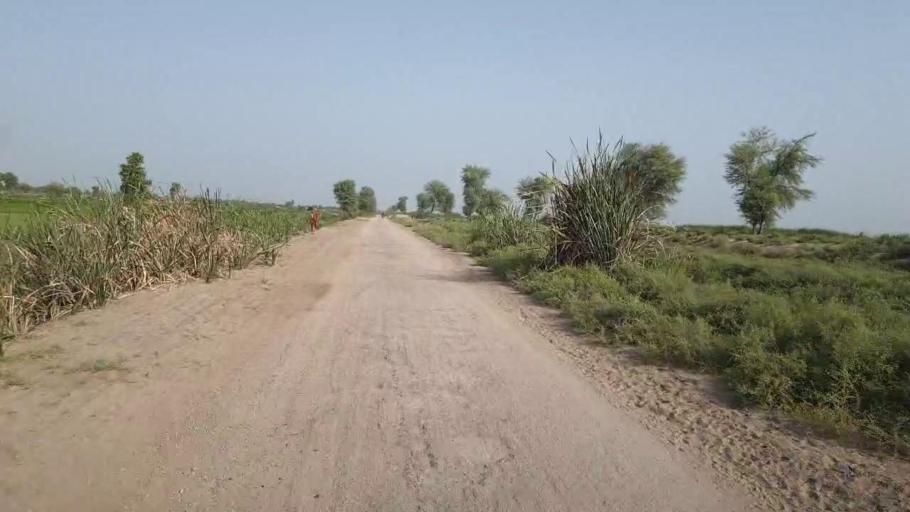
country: PK
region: Sindh
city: Daur
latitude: 26.3377
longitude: 68.1845
